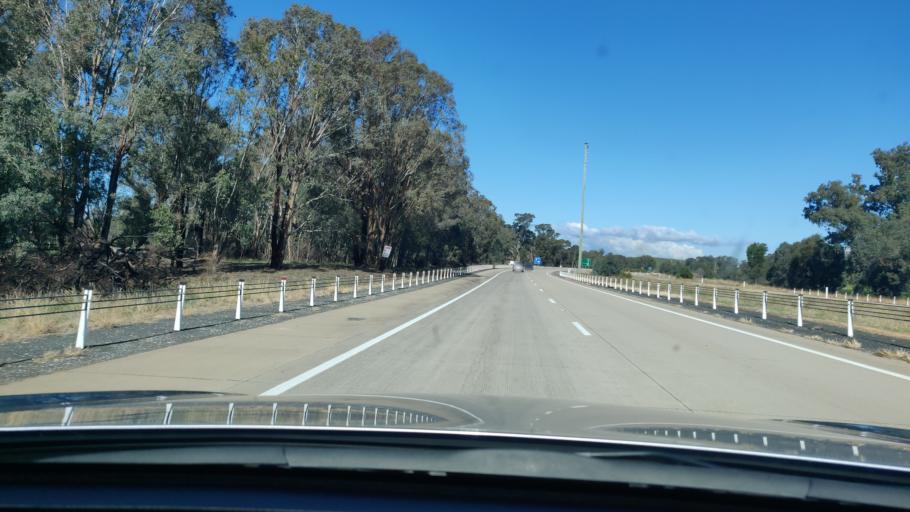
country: AU
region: New South Wales
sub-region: Wagga Wagga
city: Forest Hill
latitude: -35.2498
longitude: 147.7616
